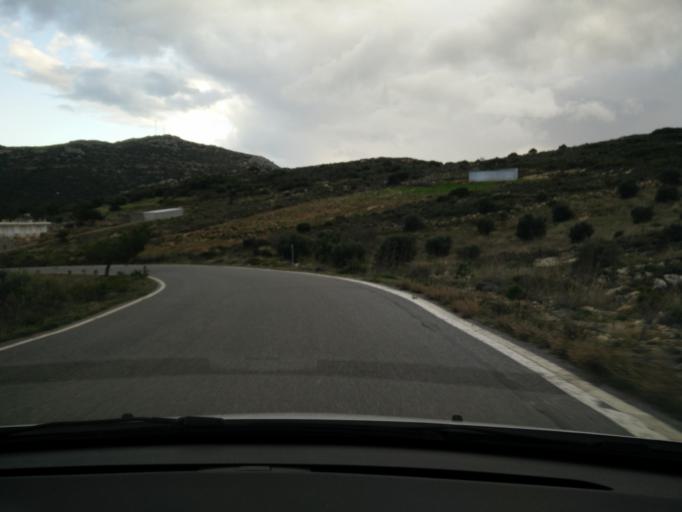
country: GR
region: Crete
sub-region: Nomos Lasithiou
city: Gra Liyia
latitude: 35.0863
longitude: 25.7061
